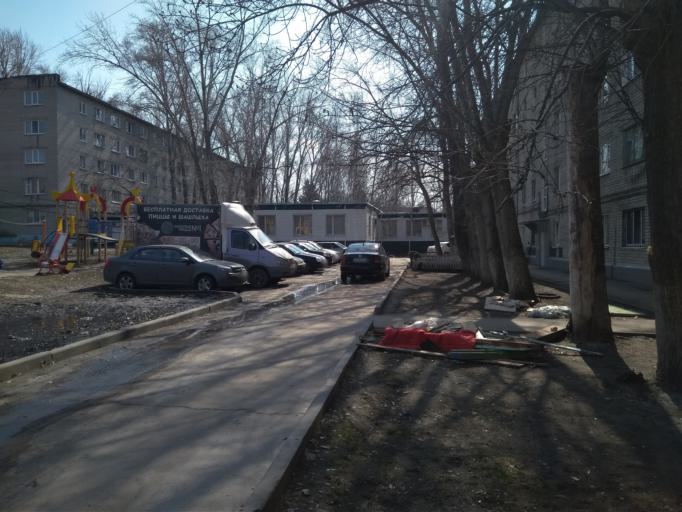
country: RU
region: Ulyanovsk
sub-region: Ulyanovskiy Rayon
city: Ulyanovsk
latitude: 54.2599
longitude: 48.3280
